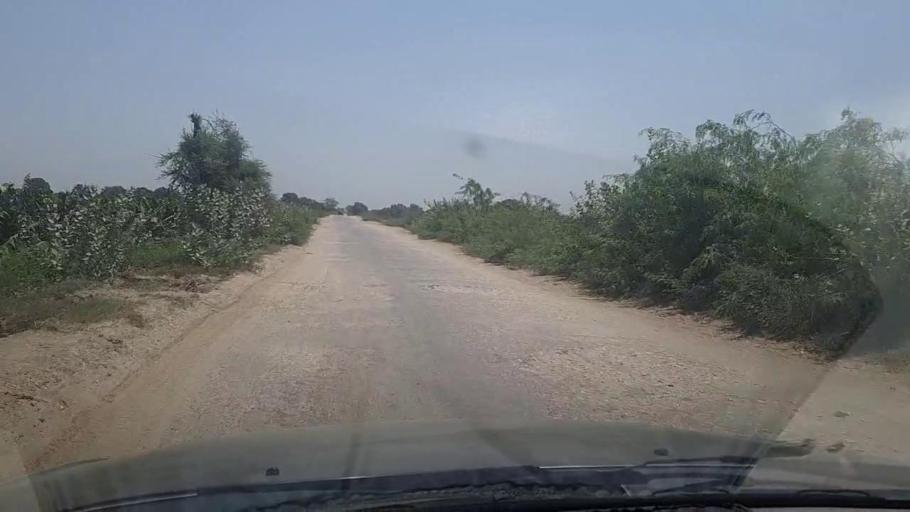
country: PK
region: Sindh
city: Tando Jam
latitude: 25.2758
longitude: 68.6211
